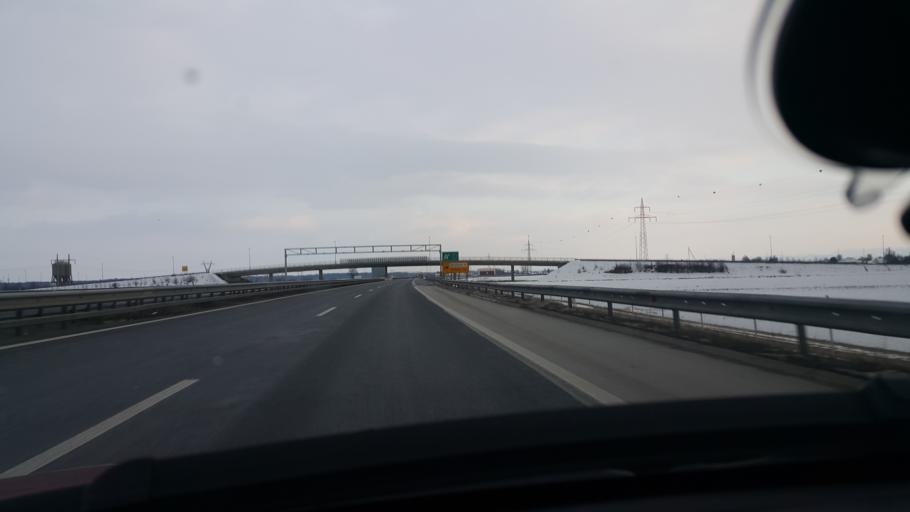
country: SI
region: Hoce-Slivnica
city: Hotinja Vas
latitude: 46.4761
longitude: 15.6719
